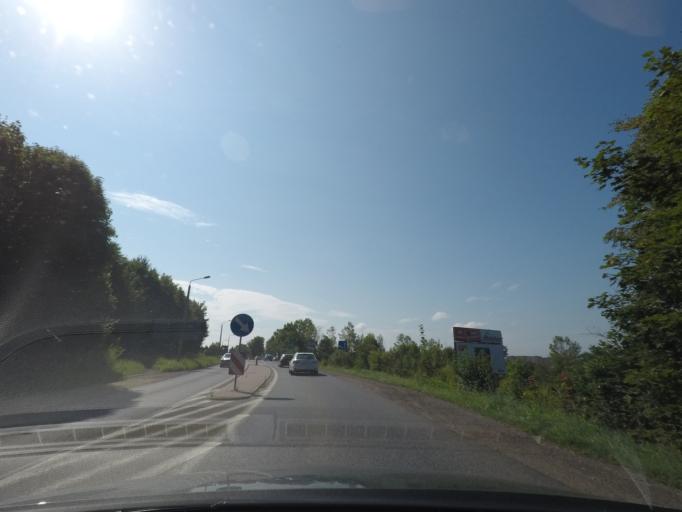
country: PL
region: Lesser Poland Voivodeship
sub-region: Powiat chrzanowski
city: Chrzanow
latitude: 50.1498
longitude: 19.3987
